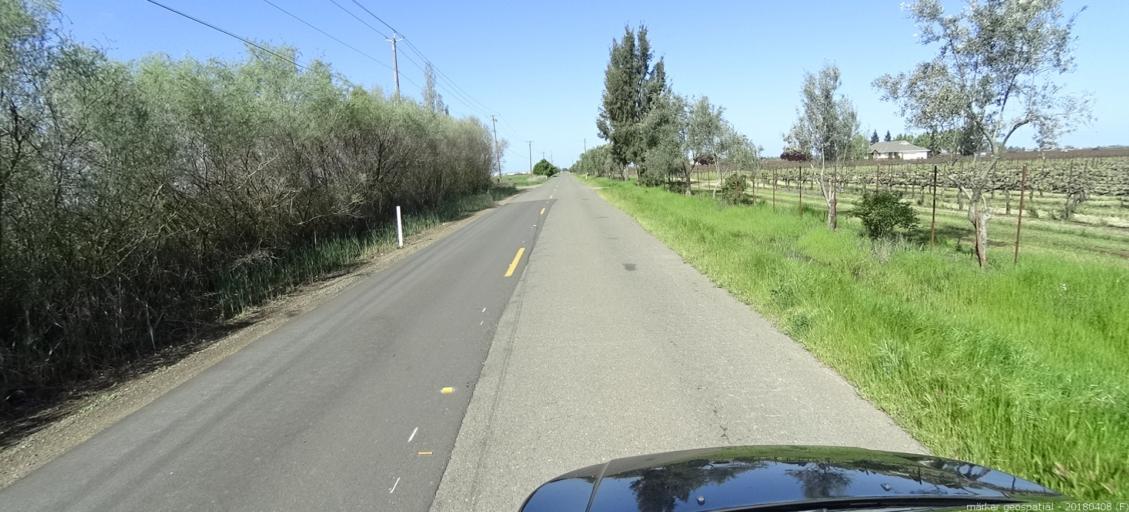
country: US
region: California
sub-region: Sacramento County
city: Elk Grove
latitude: 38.3508
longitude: -121.3795
